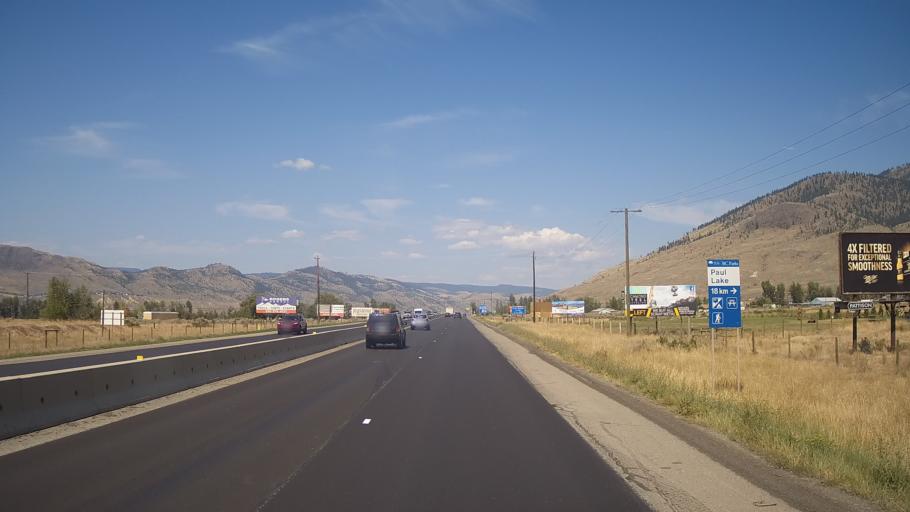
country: CA
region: British Columbia
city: Kamloops
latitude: 50.7026
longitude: -120.3267
